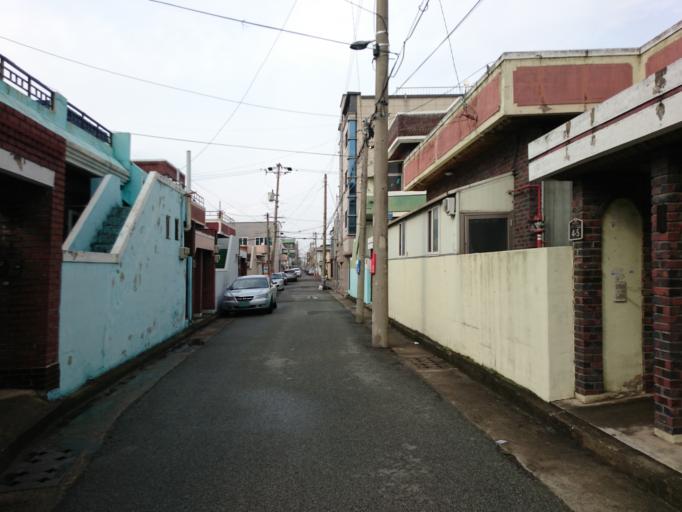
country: KR
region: Gyeongsangbuk-do
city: Pohang
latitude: 36.0244
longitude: 129.3736
